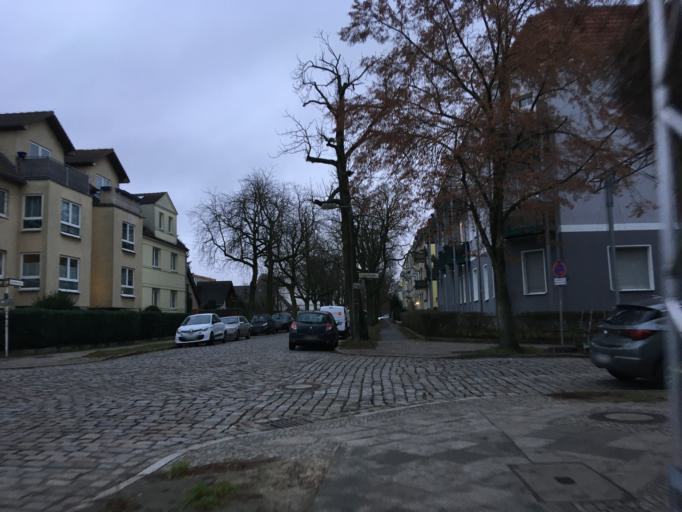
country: DE
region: Berlin
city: Niederschonhausen
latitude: 52.5898
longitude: 13.4109
